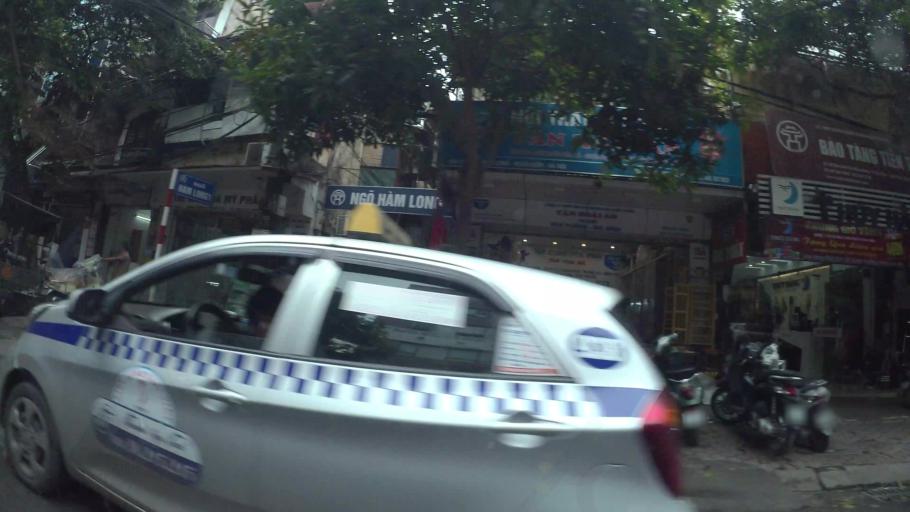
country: VN
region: Ha Noi
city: Hai BaTrung
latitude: 21.0187
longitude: 105.8540
